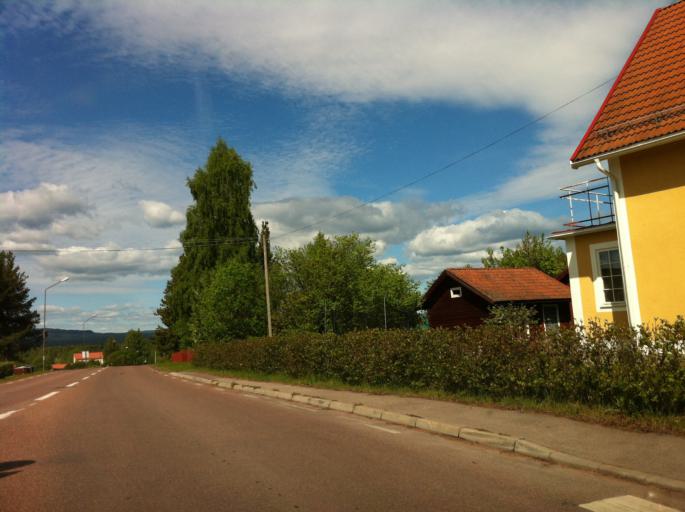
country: SE
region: Dalarna
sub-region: Mora Kommun
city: Mora
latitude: 60.9161
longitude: 14.6162
